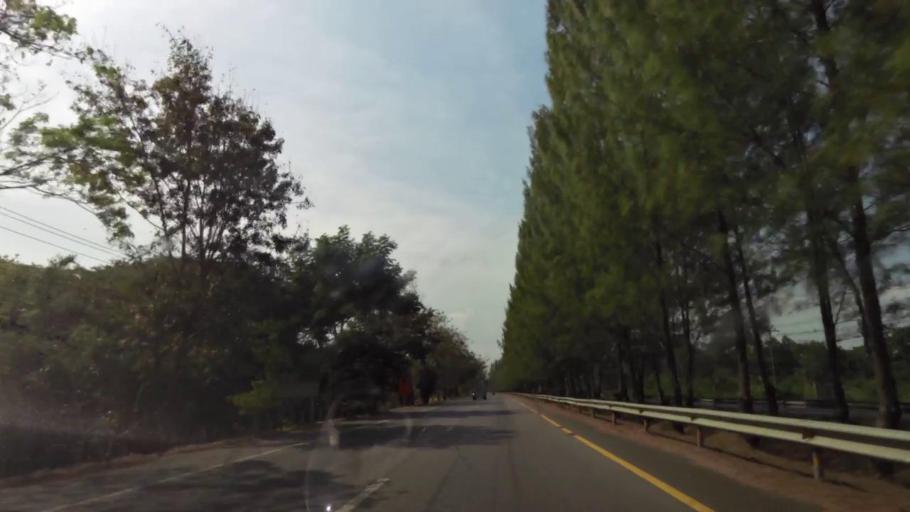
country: TH
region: Chanthaburi
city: Chanthaburi
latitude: 12.6663
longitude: 102.0990
